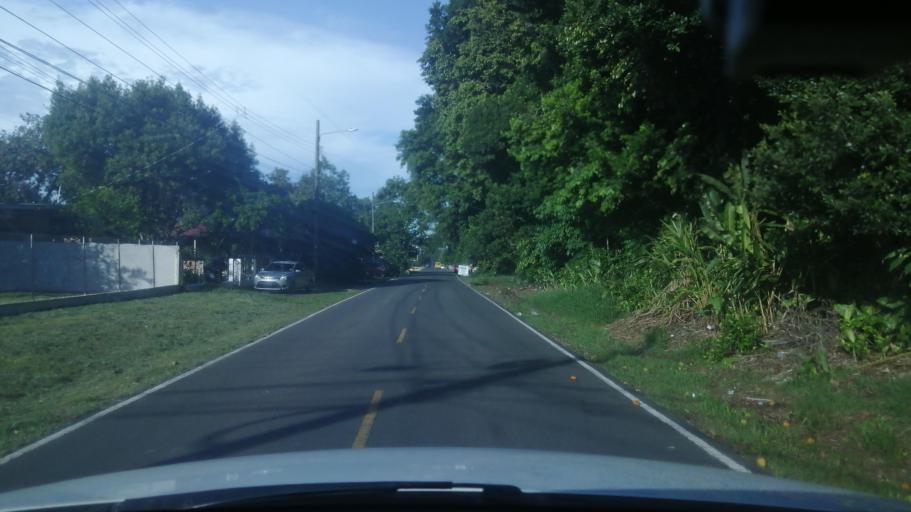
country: PA
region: Chiriqui
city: David
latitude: 8.4367
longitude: -82.4327
